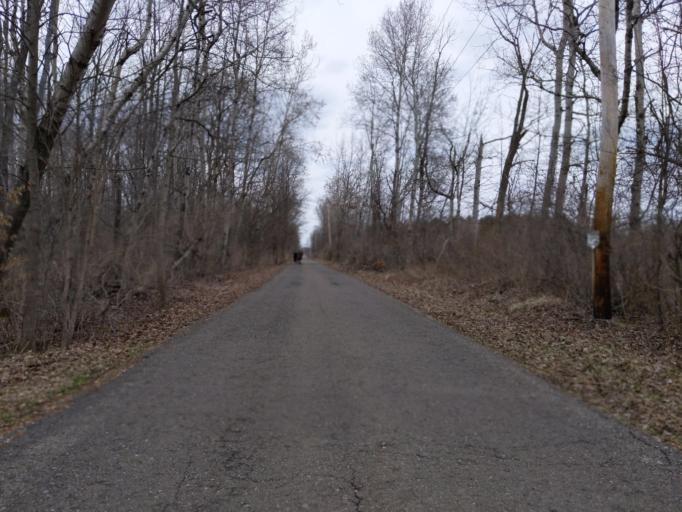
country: US
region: New York
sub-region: Tompkins County
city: Dryden
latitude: 42.5082
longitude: -76.3431
